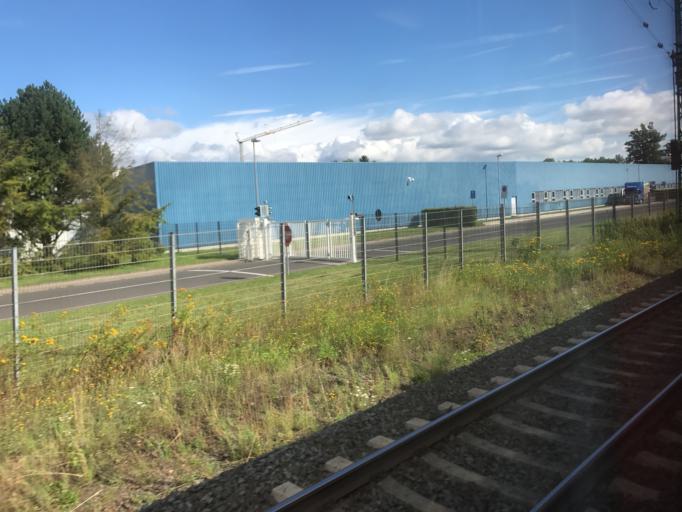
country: DE
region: Hesse
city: Lollar
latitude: 50.6514
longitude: 8.7051
